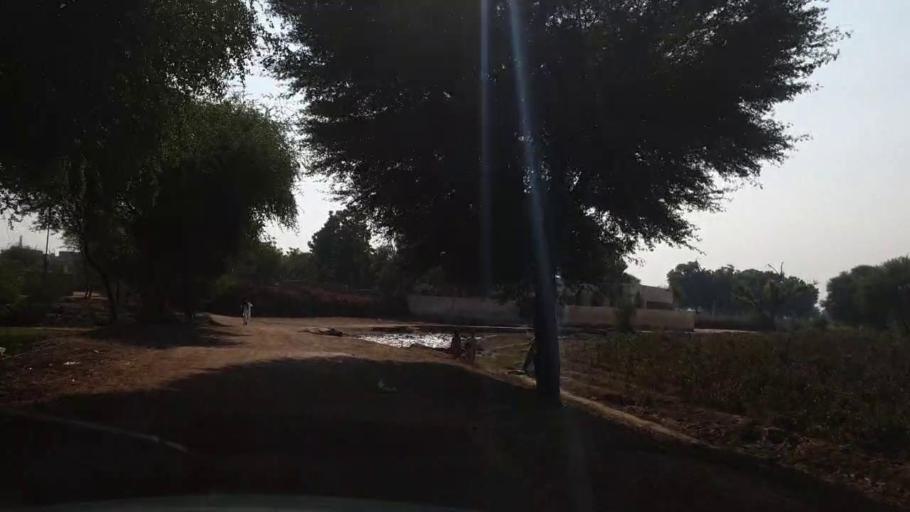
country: PK
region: Sindh
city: Bhan
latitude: 26.5311
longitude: 67.7632
